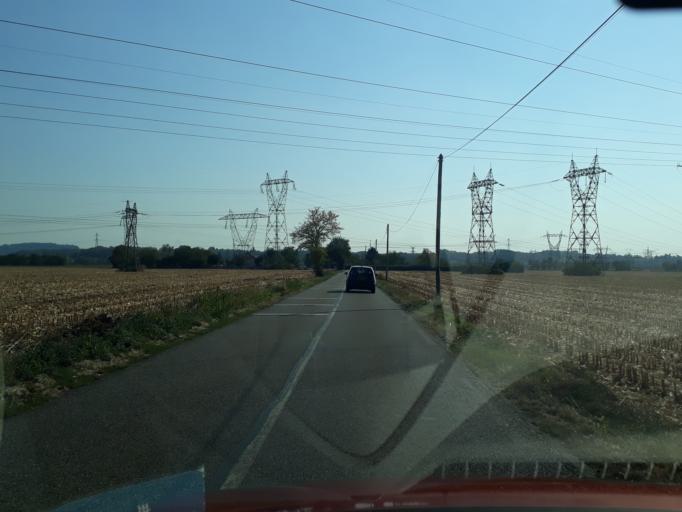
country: FR
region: Rhone-Alpes
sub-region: Departement du Rhone
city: Toussieu
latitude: 45.6828
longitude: 4.9832
